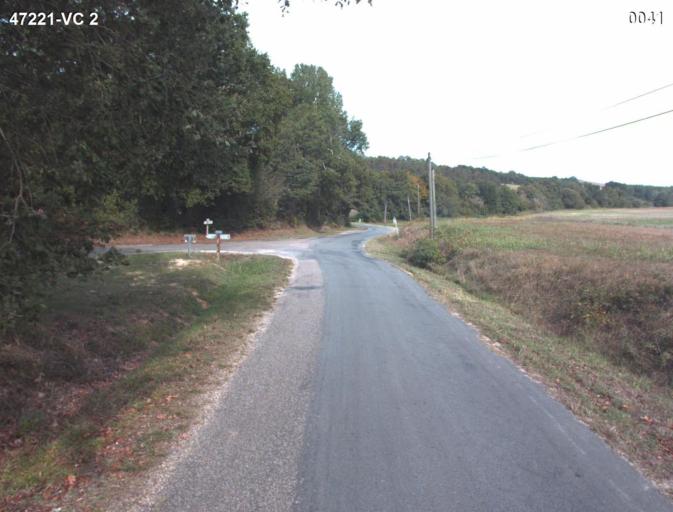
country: FR
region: Aquitaine
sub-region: Departement du Lot-et-Garonne
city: Mezin
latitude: 44.1094
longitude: 0.2375
